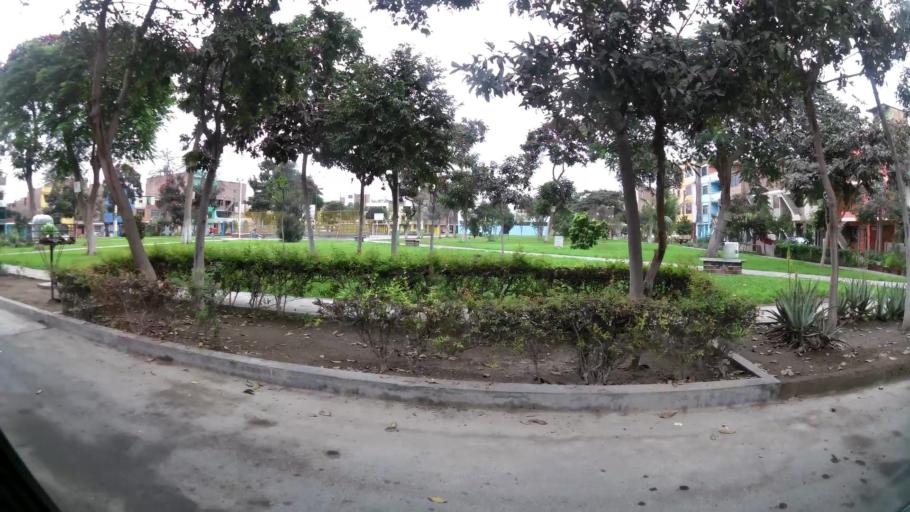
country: PE
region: Lima
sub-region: Lima
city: Independencia
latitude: -11.9755
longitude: -77.0706
